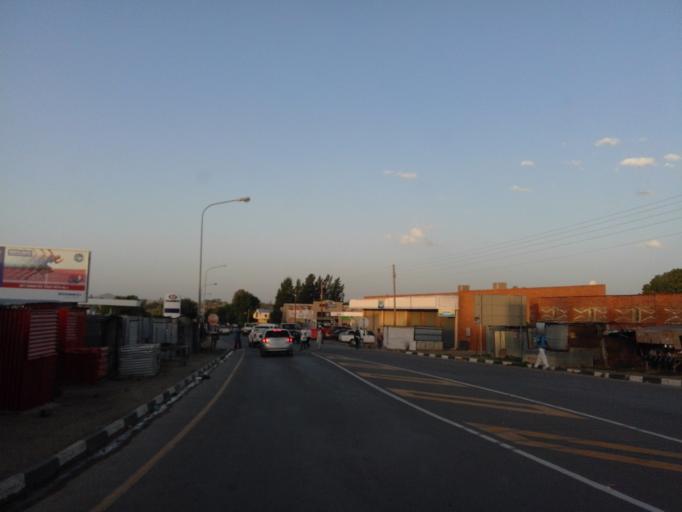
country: LS
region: Mafeteng
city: Mafeteng
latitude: -29.8224
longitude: 27.2442
